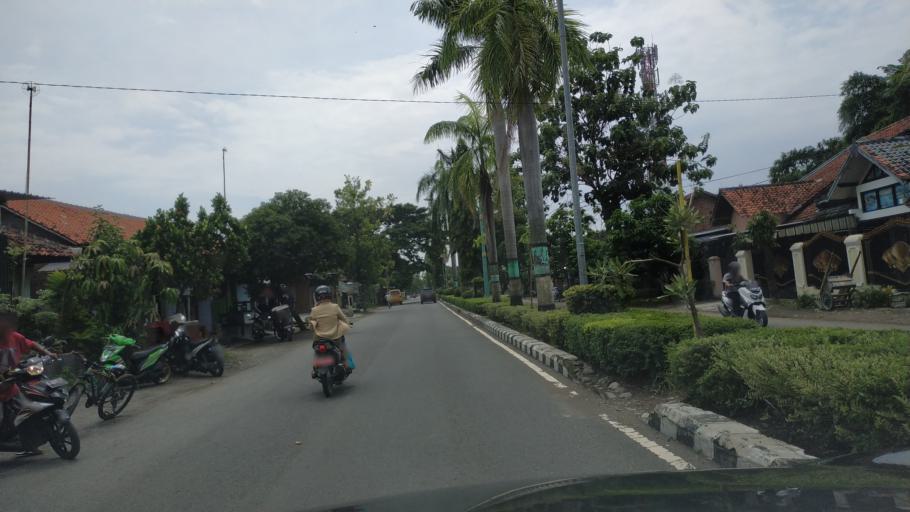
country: ID
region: Central Java
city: Slawi
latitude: -6.9849
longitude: 109.1270
